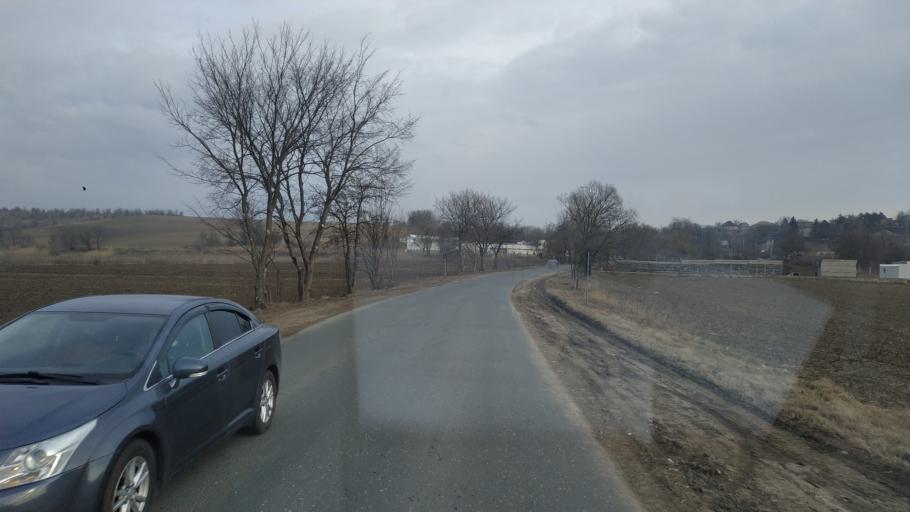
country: MD
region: Chisinau
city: Singera
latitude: 46.9243
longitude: 29.0473
